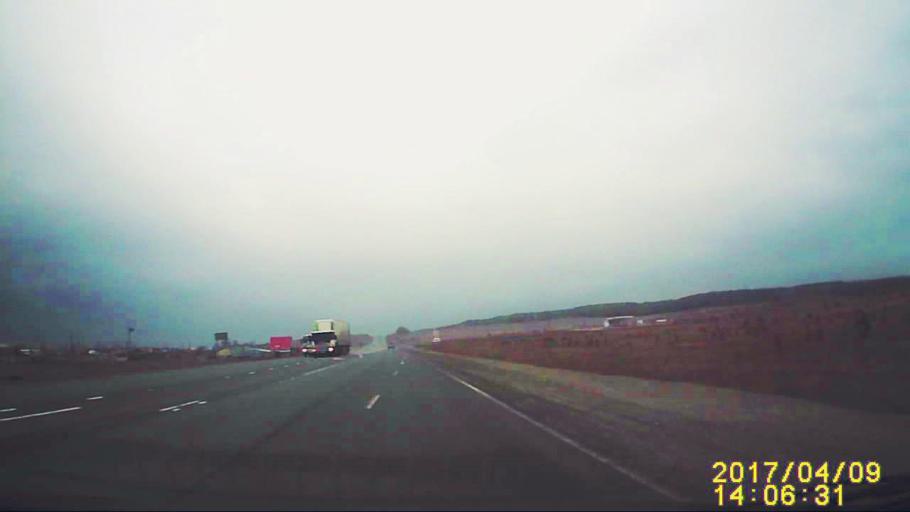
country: RU
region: Ulyanovsk
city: Silikatnyy
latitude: 54.0034
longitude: 48.2208
